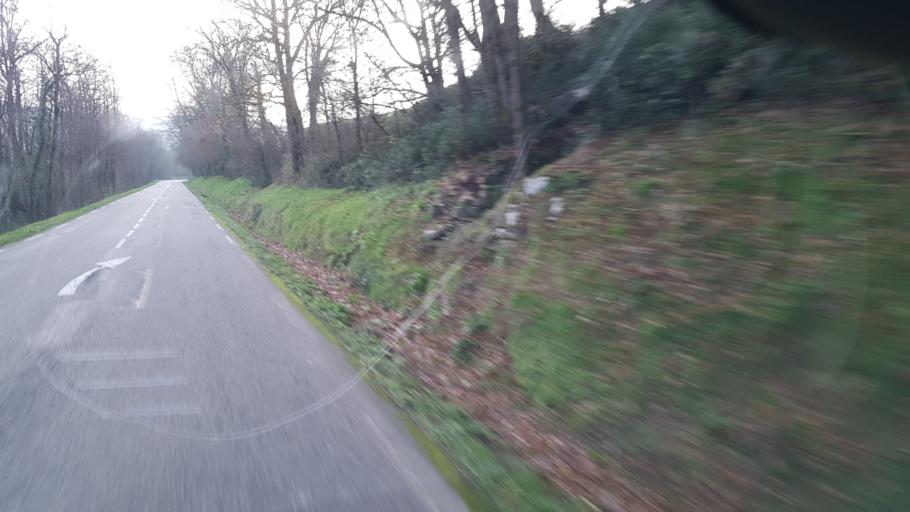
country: FR
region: Midi-Pyrenees
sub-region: Departement du Tarn-et-Garonne
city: Montricoux
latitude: 44.0682
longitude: 1.6544
